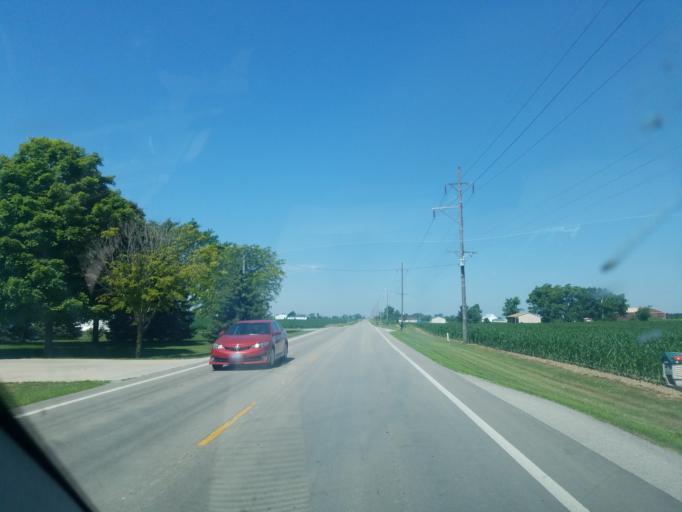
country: US
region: Ohio
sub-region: Auglaize County
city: New Bremen
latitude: 40.4368
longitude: -84.4085
